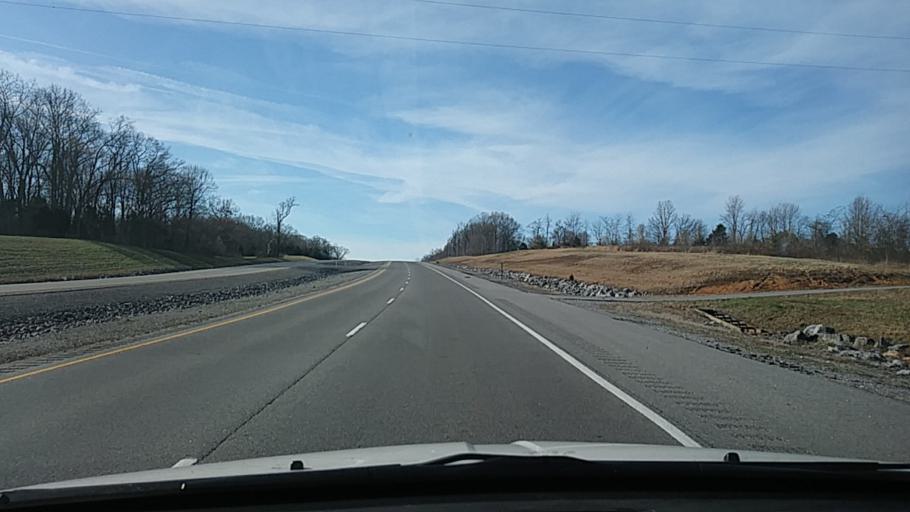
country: US
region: Tennessee
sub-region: Sumner County
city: Portland
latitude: 36.5370
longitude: -86.5086
